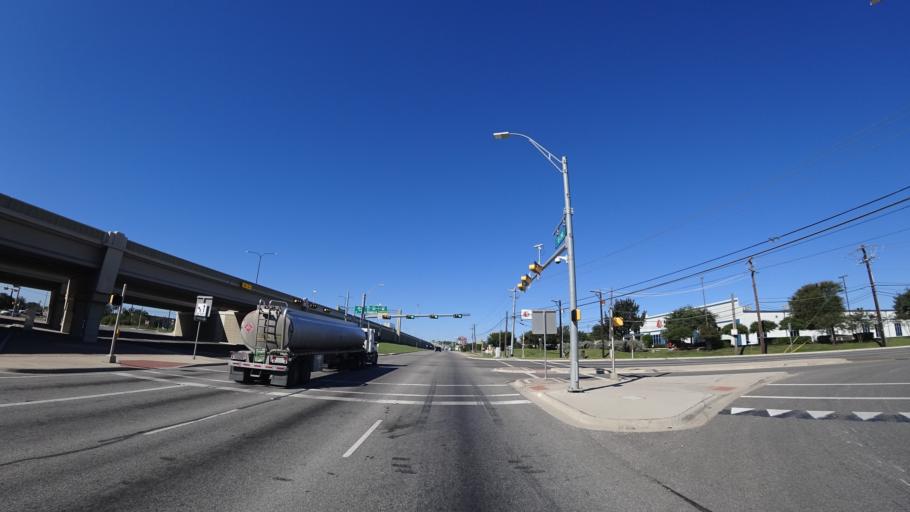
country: US
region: Texas
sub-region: Travis County
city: Manor
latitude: 30.3291
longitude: -97.6543
